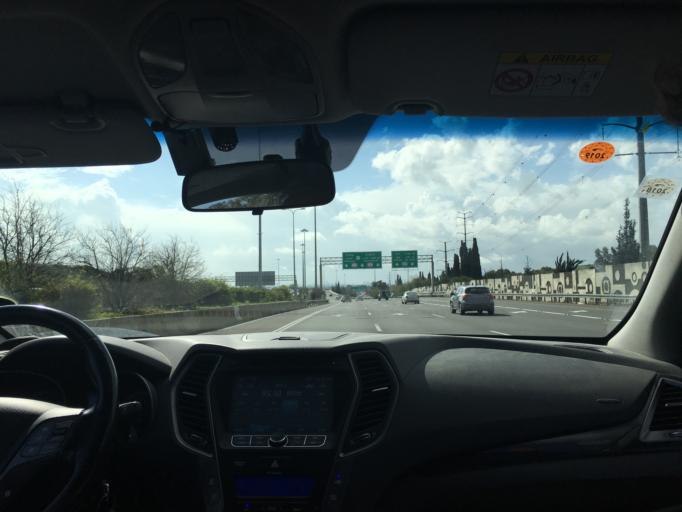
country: IL
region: Tel Aviv
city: Azor
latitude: 32.0433
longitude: 34.8296
